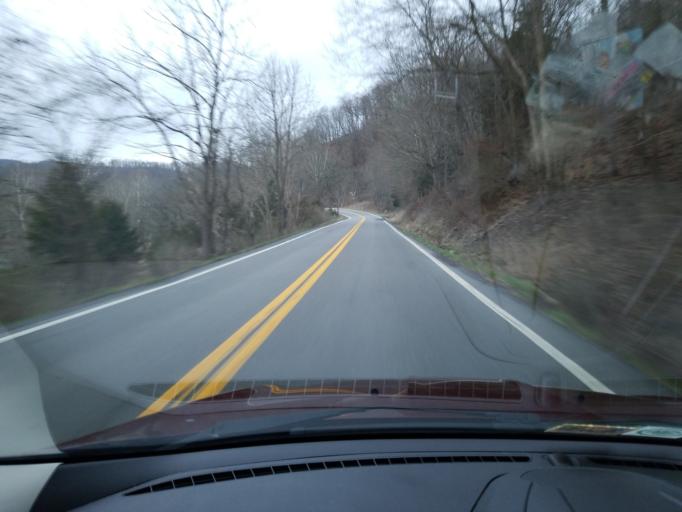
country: US
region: West Virginia
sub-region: Monroe County
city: Union
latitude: 37.5629
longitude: -80.5690
